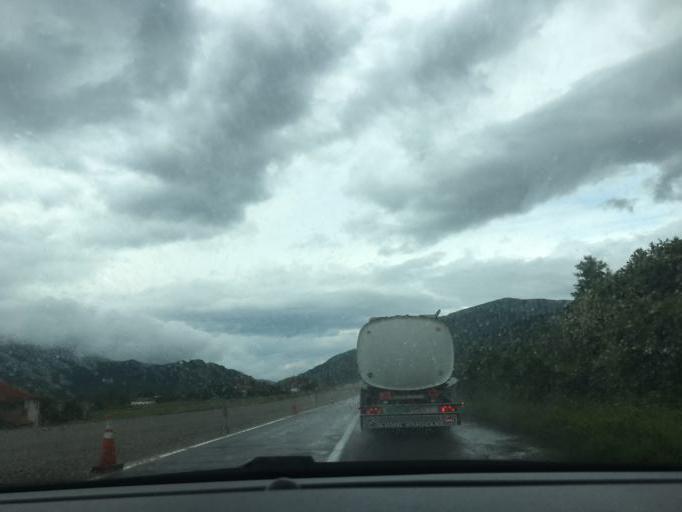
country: MK
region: Debarca
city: Meseista
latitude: 41.2397
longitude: 20.7690
